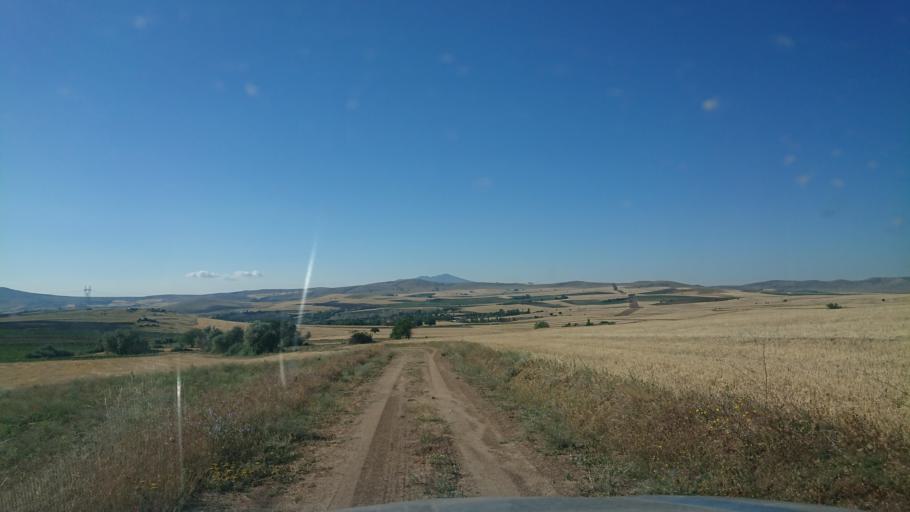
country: TR
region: Aksaray
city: Agacoren
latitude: 38.8347
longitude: 33.9388
